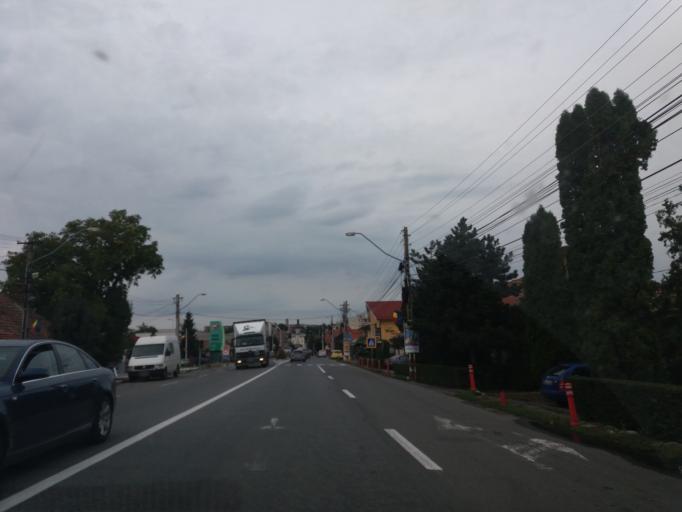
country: RO
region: Mures
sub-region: Municipiul Reghin
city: Reghin
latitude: 46.7701
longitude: 24.7036
